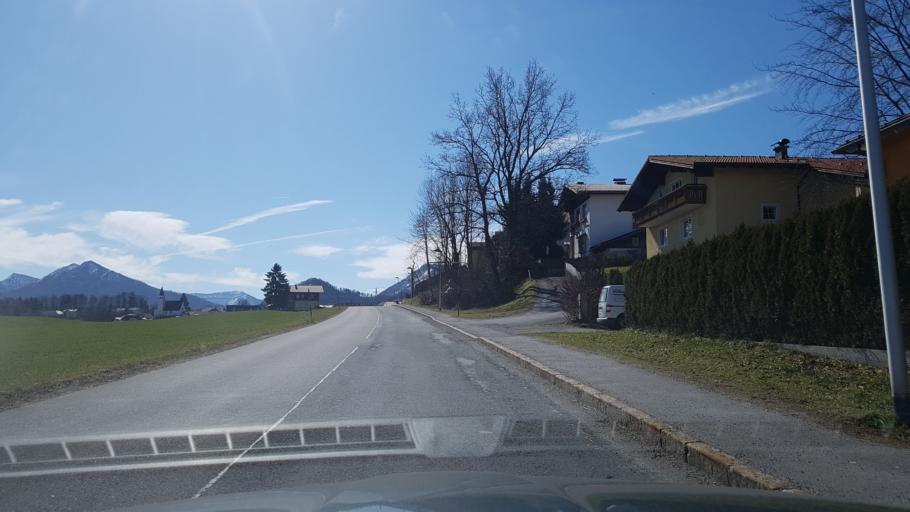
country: AT
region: Salzburg
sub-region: Politischer Bezirk Salzburg-Umgebung
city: Koppl
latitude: 47.8139
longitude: 13.1537
